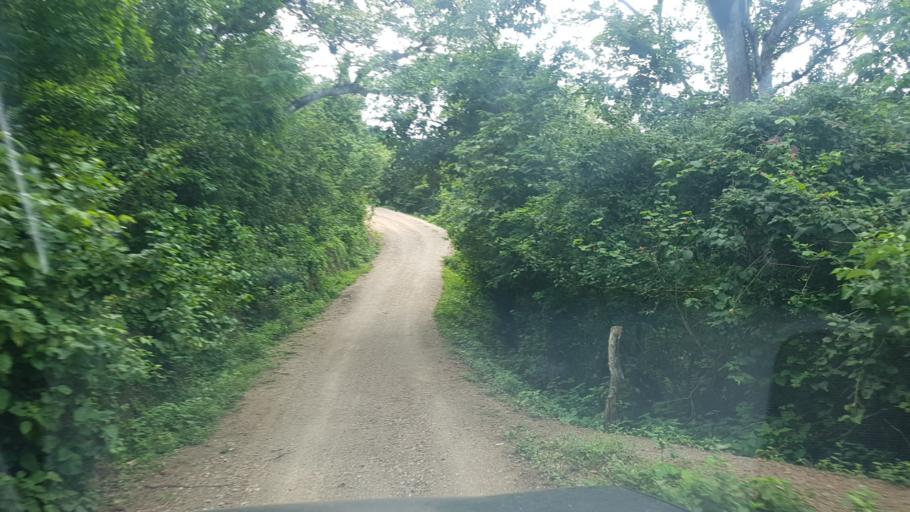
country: NI
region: Nueva Segovia
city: Ocotal
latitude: 13.5994
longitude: -86.4241
